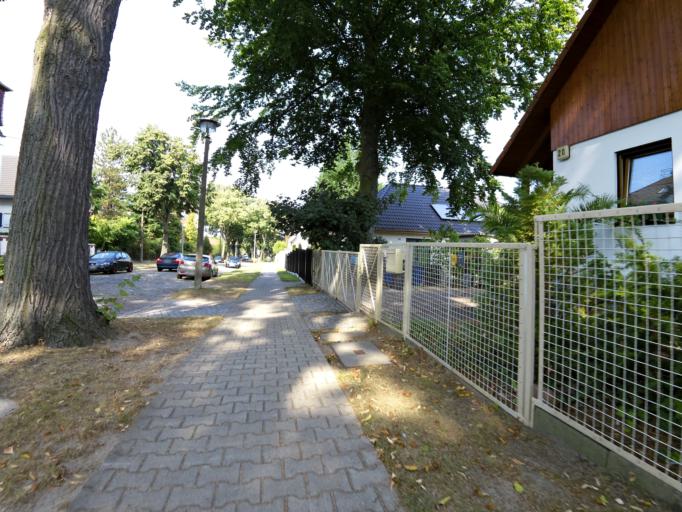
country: DE
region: Berlin
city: Grunau
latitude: 52.4126
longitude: 13.5603
